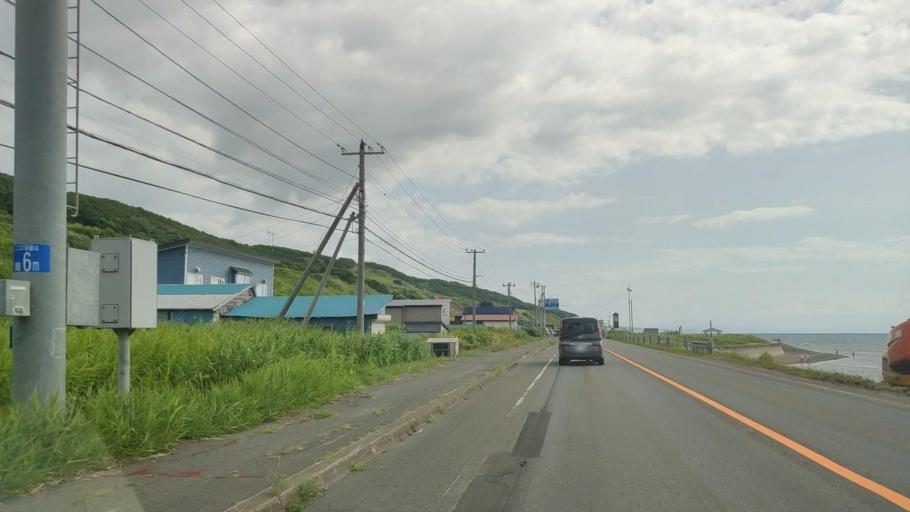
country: JP
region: Hokkaido
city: Rumoi
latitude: 44.1394
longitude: 141.6542
